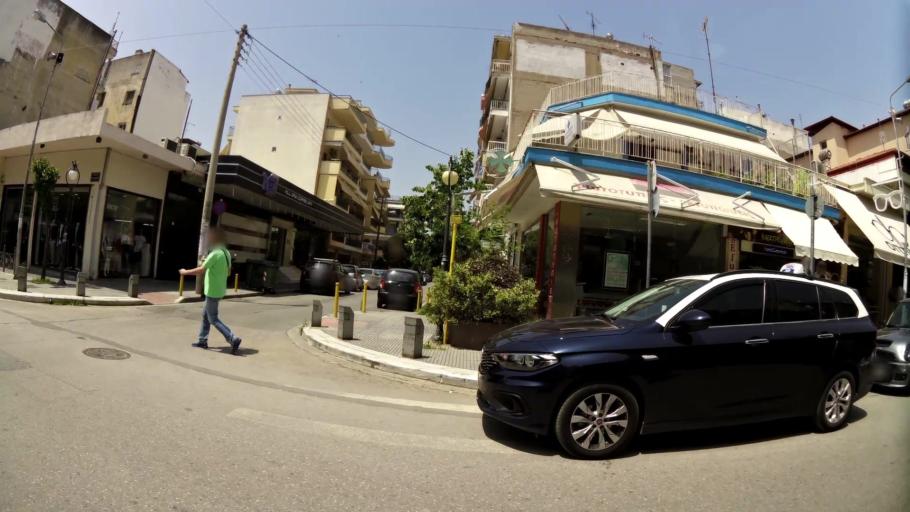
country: GR
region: Central Macedonia
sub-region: Nomos Thessalonikis
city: Menemeni
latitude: 40.6703
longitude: 22.8942
